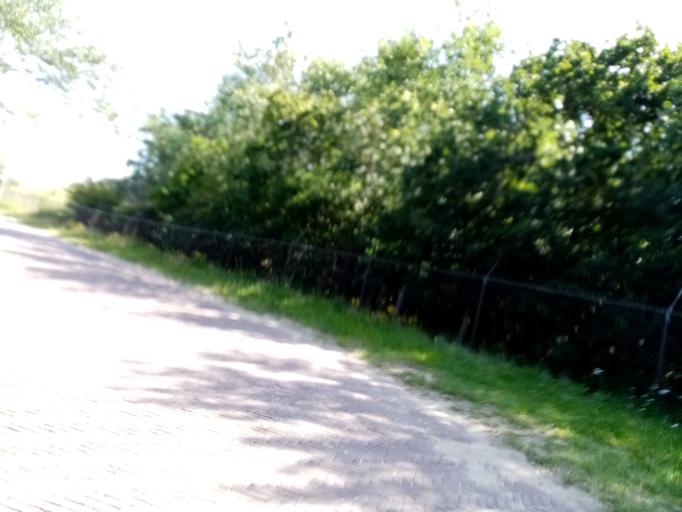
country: NL
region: South Holland
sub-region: Gemeente Noordwijk
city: Noordwijk-Binnen
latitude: 52.2318
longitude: 4.4274
